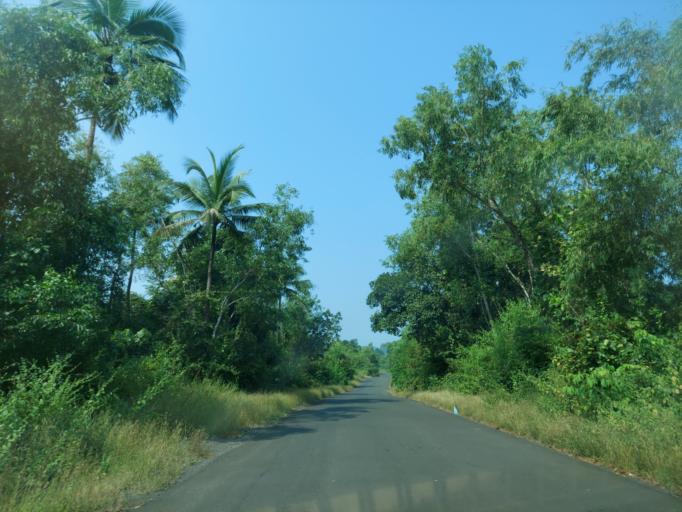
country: IN
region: Maharashtra
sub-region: Sindhudurg
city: Kudal
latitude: 15.9757
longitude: 73.6208
